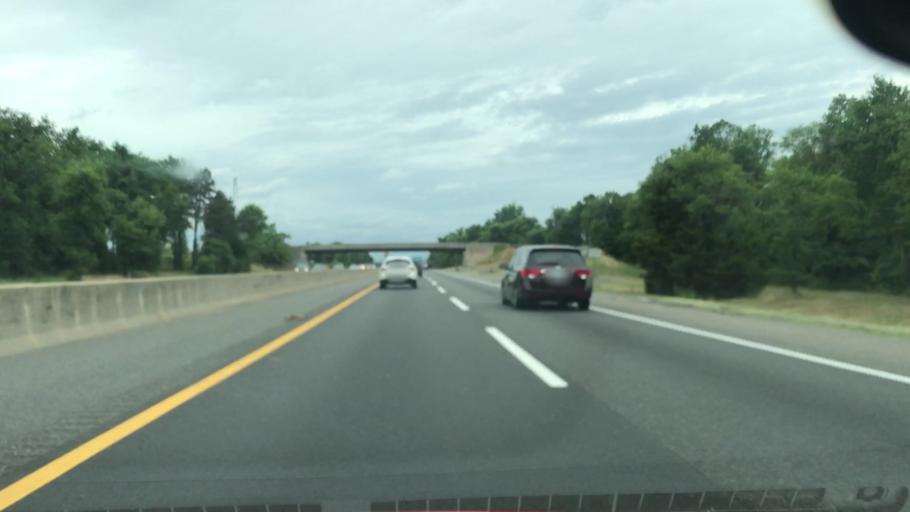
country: US
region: New Jersey
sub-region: Gloucester County
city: Swedesboro
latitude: 39.7595
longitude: -75.2668
